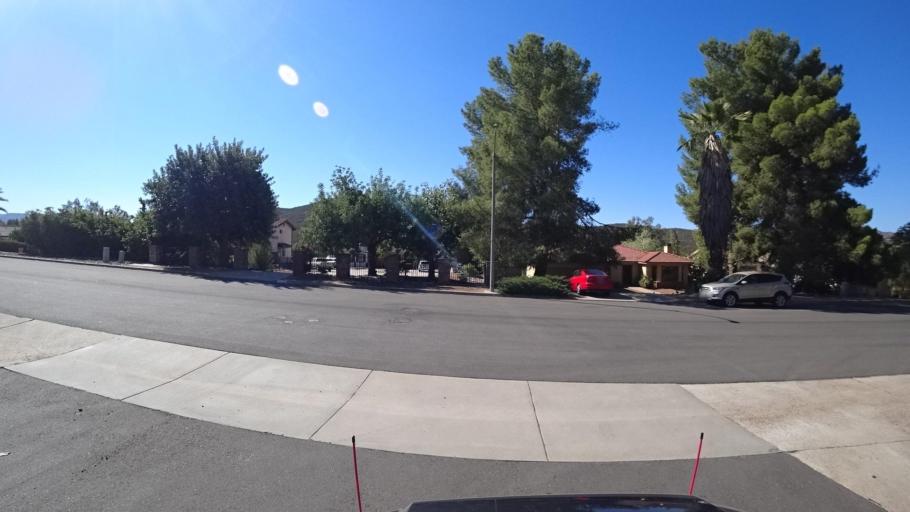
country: US
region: California
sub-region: San Diego County
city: San Diego Country Estates
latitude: 33.0013
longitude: -116.7638
